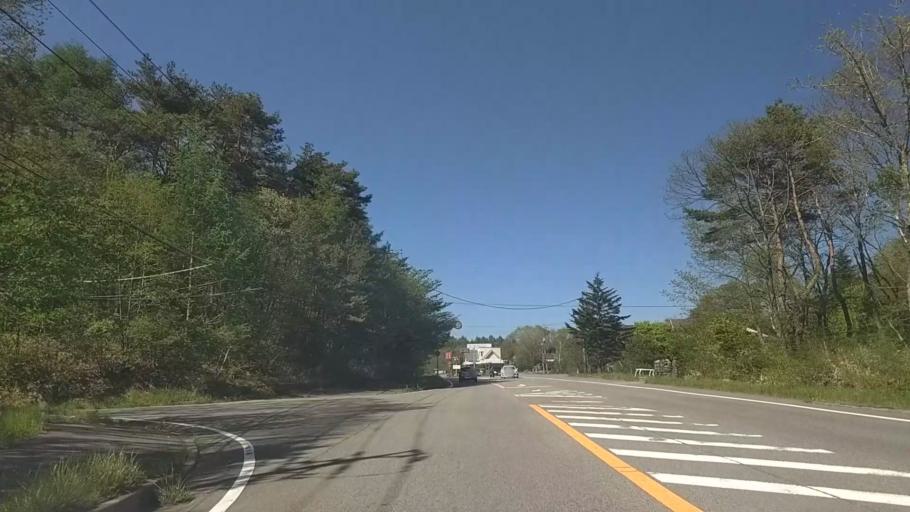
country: JP
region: Yamanashi
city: Nirasaki
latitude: 35.9276
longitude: 138.4420
